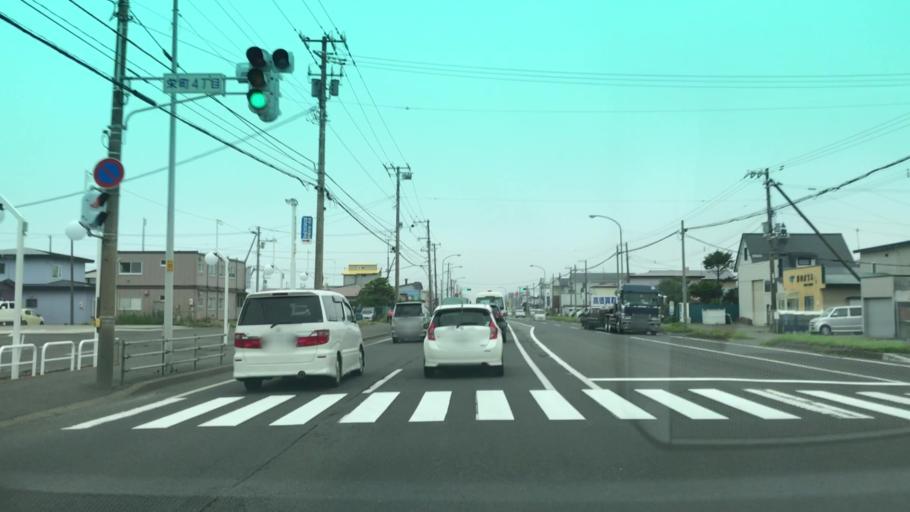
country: JP
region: Hokkaido
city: Muroran
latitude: 42.3784
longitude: 141.0711
